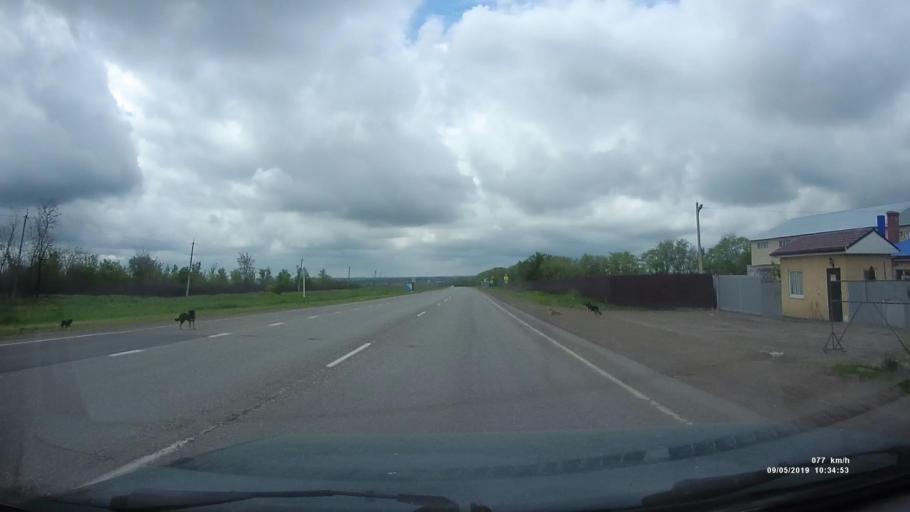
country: RU
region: Rostov
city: Peshkovo
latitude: 47.0493
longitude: 39.4167
